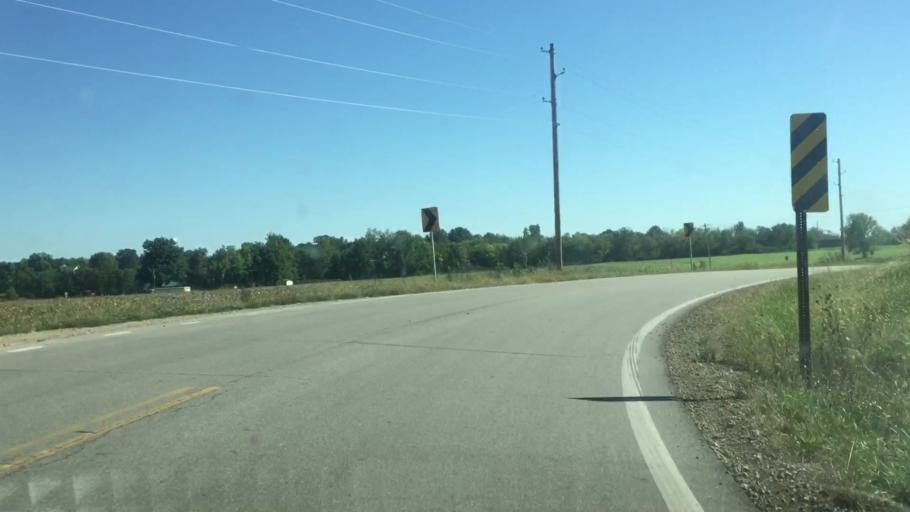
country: US
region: Kansas
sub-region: Brown County
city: Horton
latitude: 39.5946
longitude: -95.6204
